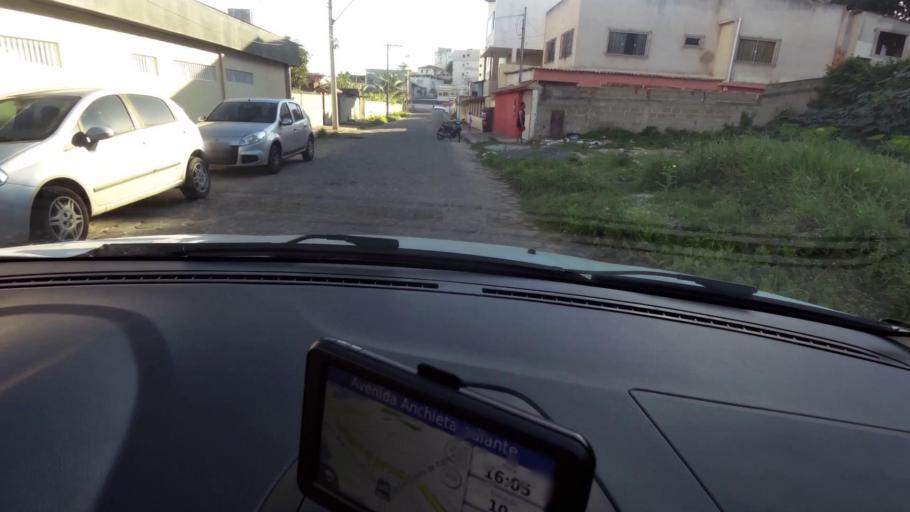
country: BR
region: Espirito Santo
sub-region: Guarapari
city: Guarapari
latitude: -20.6781
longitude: -40.5030
